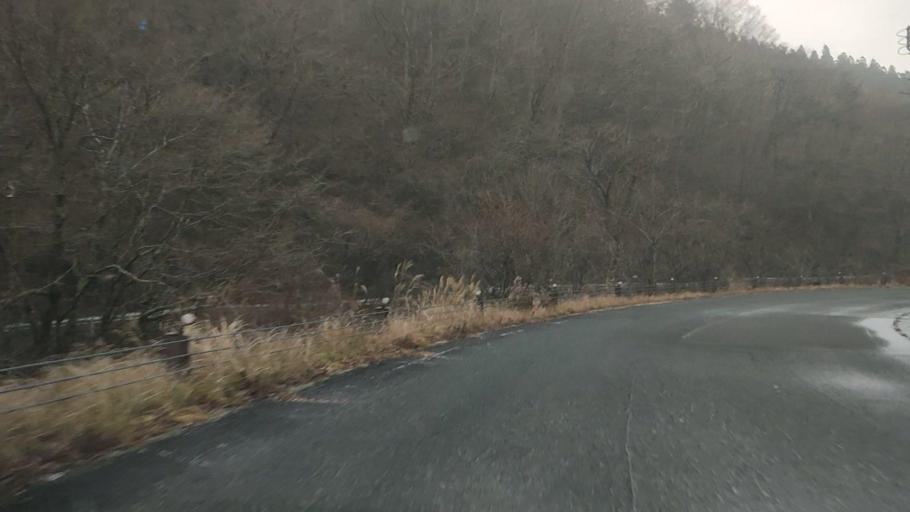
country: JP
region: Kumamoto
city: Matsubase
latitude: 32.5651
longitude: 130.9132
